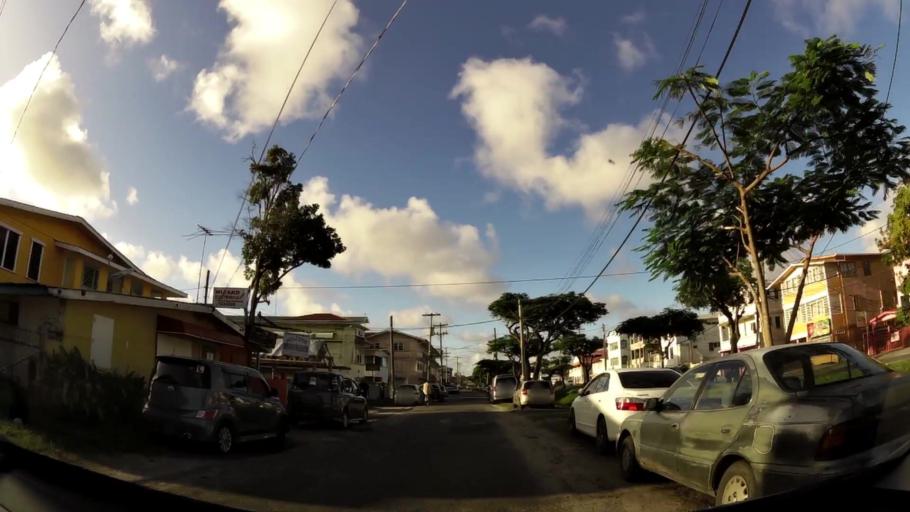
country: GY
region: Demerara-Mahaica
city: Georgetown
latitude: 6.8140
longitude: -58.1580
